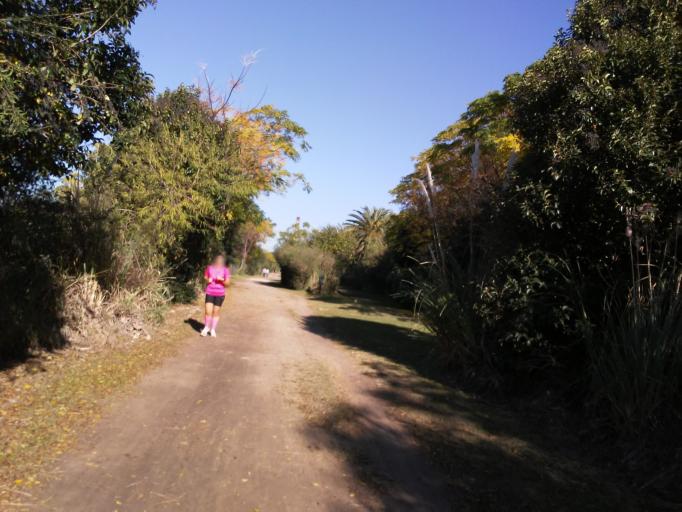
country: AR
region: Buenos Aires F.D.
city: Buenos Aires
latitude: -34.6122
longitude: -58.3407
